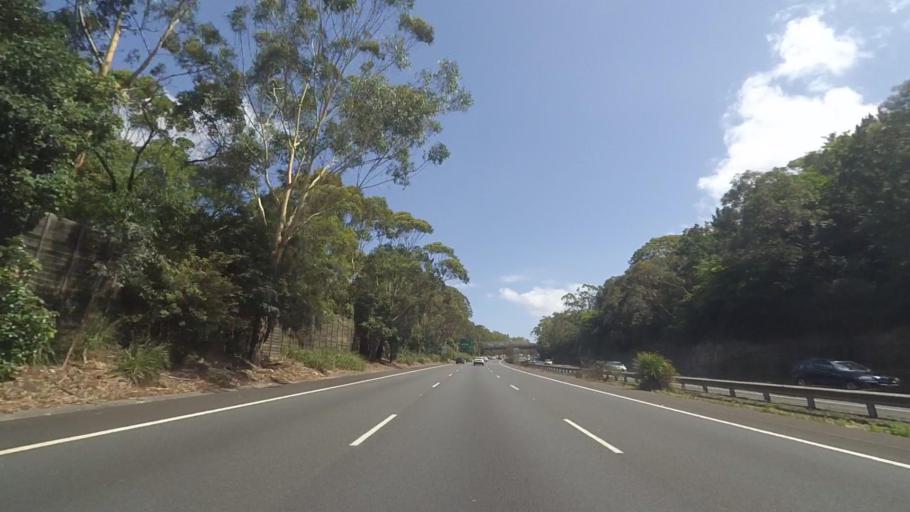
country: AU
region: New South Wales
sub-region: Ku-ring-gai
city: North Wahroonga
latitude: -33.7060
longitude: 151.1180
